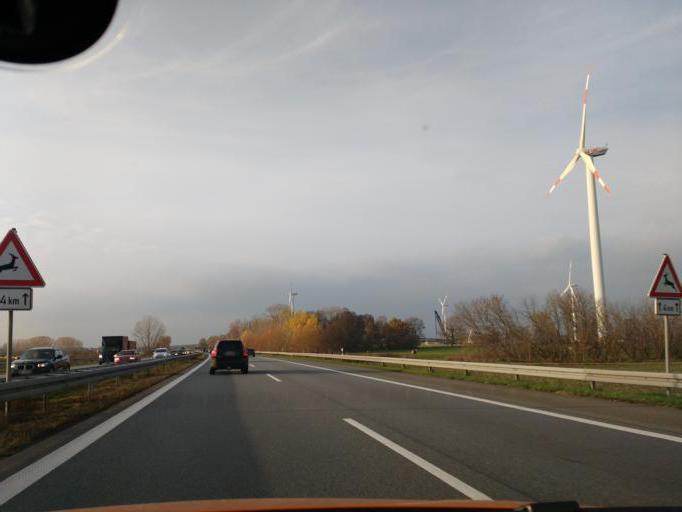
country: DE
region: Brandenburg
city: Walsleben
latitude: 52.9342
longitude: 12.6971
